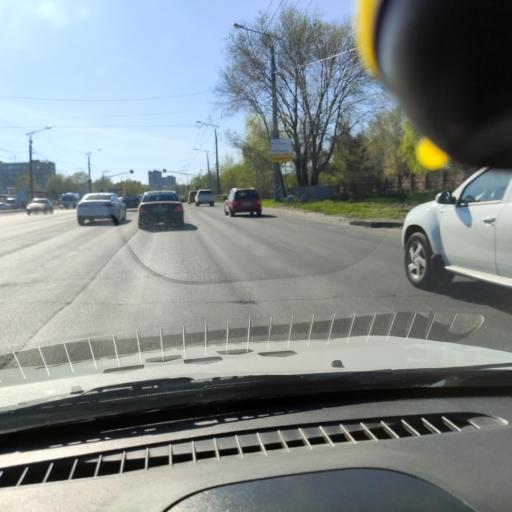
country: RU
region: Samara
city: Zhigulevsk
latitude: 53.4872
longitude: 49.4915
